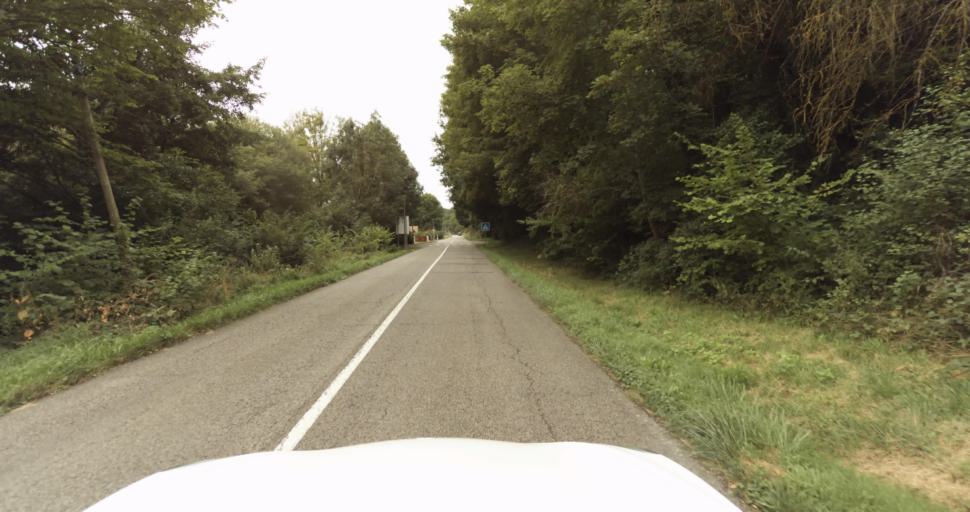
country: FR
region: Haute-Normandie
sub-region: Departement de l'Eure
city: Saint-Sebastien-de-Morsent
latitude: 48.9986
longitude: 1.0640
